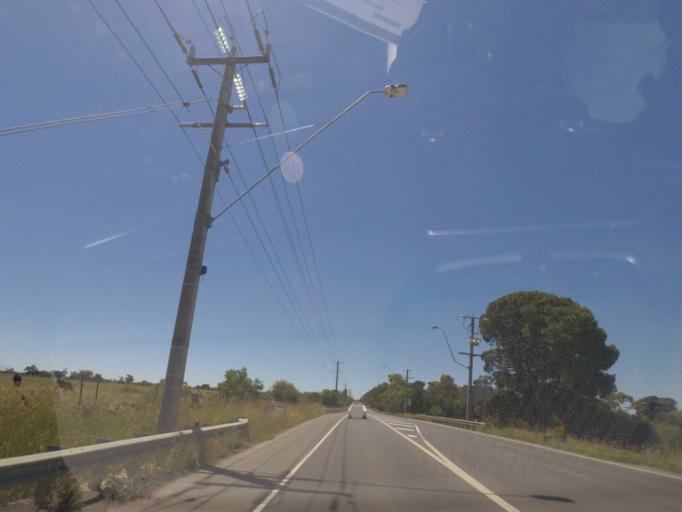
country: AU
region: Victoria
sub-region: Whittlesea
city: Epping
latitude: -37.6078
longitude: 145.0315
